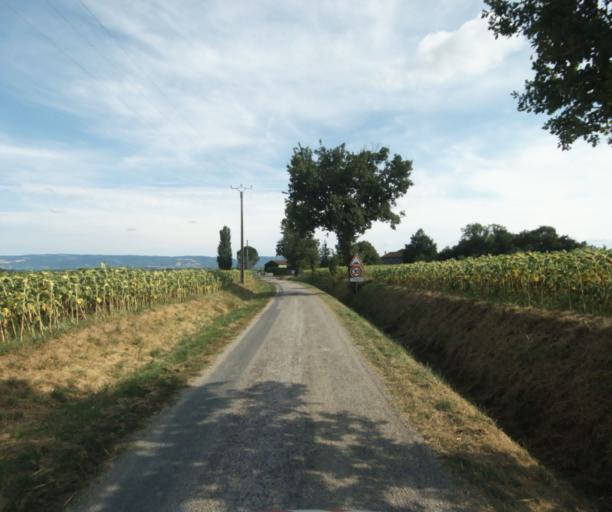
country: FR
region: Midi-Pyrenees
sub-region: Departement du Tarn
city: Puylaurens
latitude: 43.5321
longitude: 1.9911
